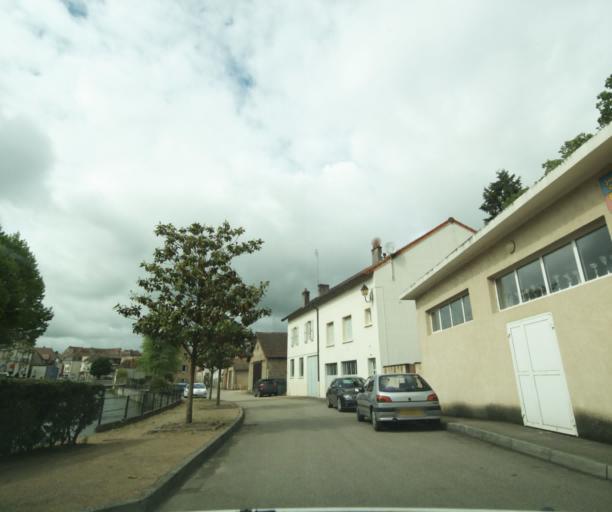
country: FR
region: Bourgogne
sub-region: Departement de Saone-et-Loire
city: Charolles
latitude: 46.4319
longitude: 4.2759
